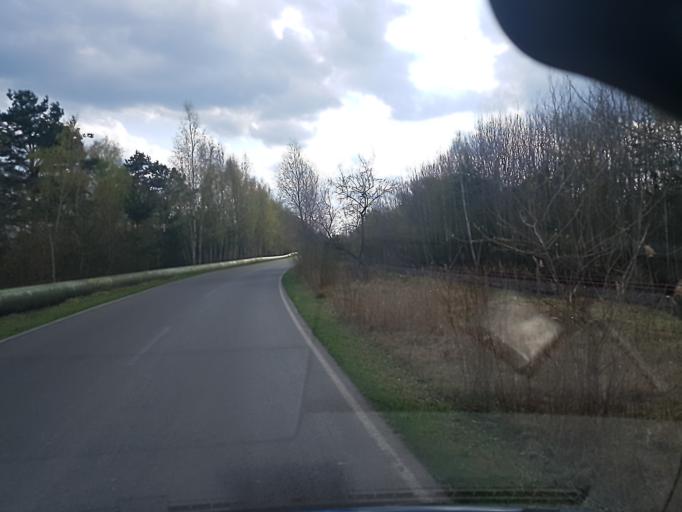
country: DE
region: Saxony-Anhalt
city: Grafenhainichen
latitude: 51.7491
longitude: 12.4366
